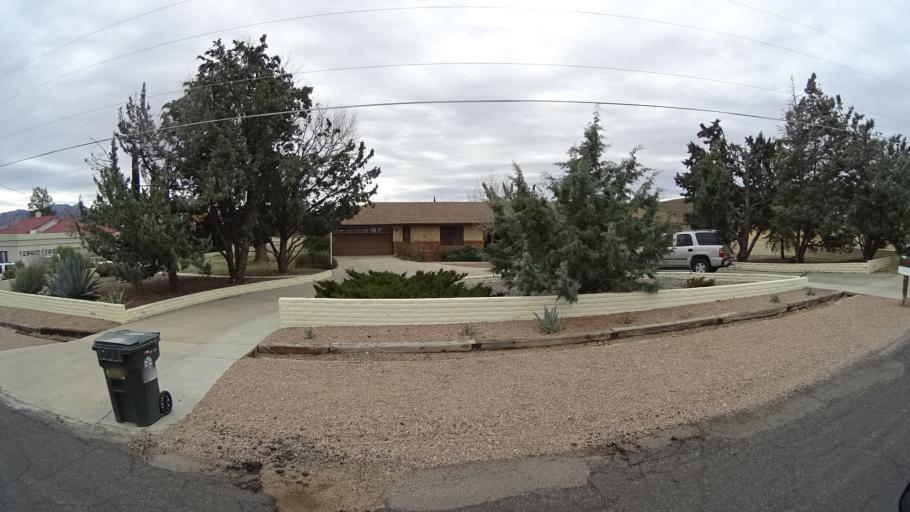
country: US
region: Arizona
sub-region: Mohave County
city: New Kingman-Butler
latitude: 35.2341
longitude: -114.0477
